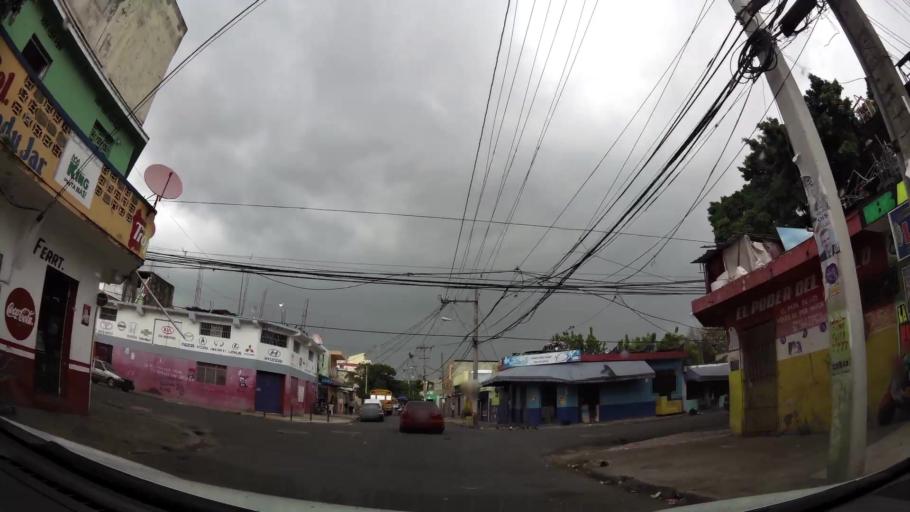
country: DO
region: Nacional
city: San Carlos
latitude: 18.4908
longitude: -69.9056
